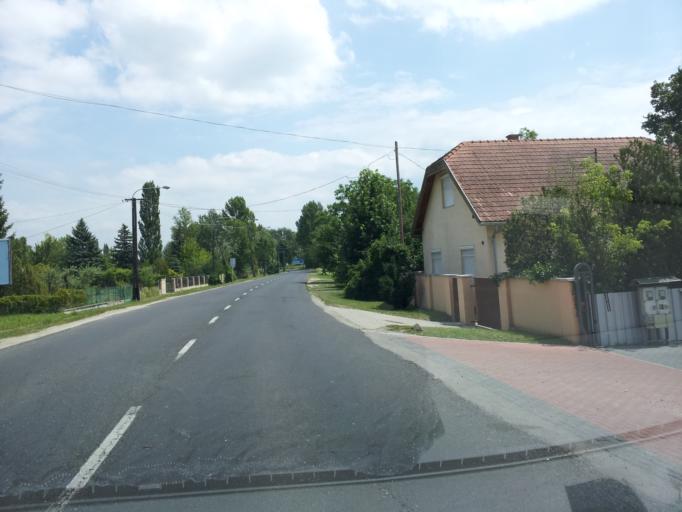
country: HU
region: Veszprem
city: Balatonkenese
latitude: 47.0332
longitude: 18.0980
